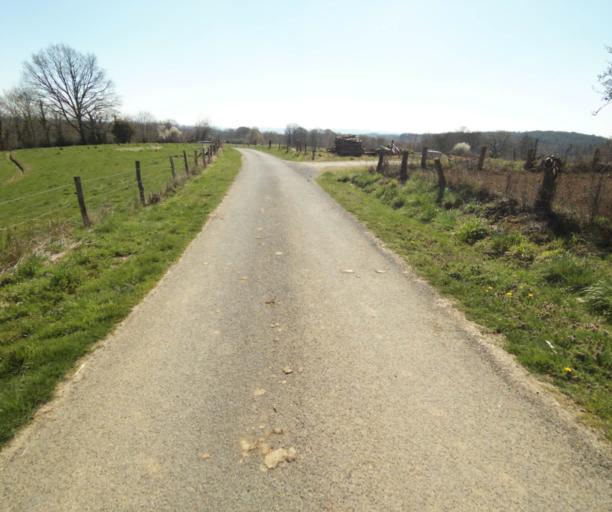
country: FR
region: Limousin
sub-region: Departement de la Correze
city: Saint-Clement
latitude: 45.3287
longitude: 1.6908
